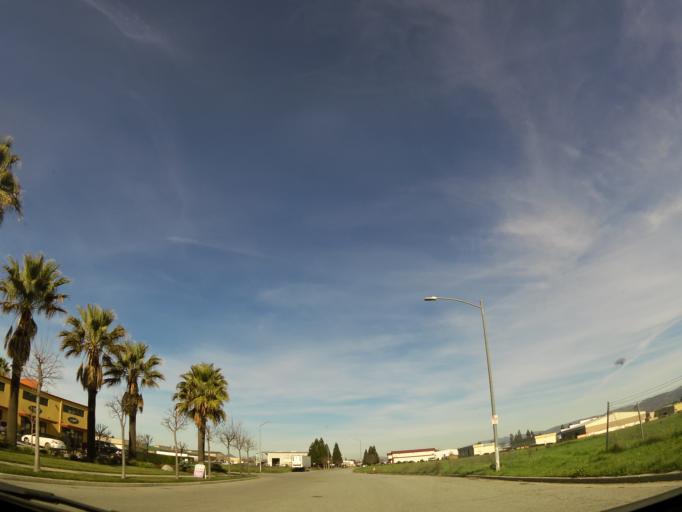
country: US
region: California
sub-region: Santa Clara County
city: Gilroy
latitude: 37.0239
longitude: -121.5735
